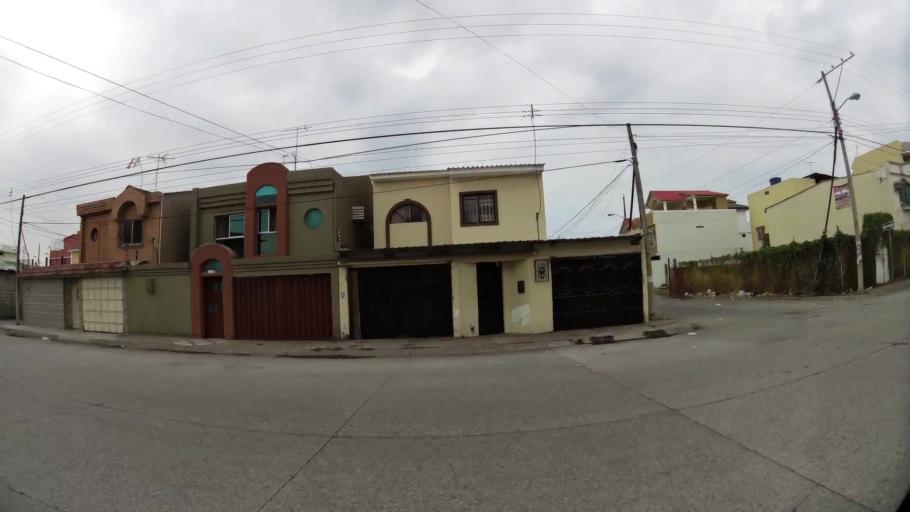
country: EC
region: Guayas
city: Eloy Alfaro
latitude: -2.1312
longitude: -79.8839
